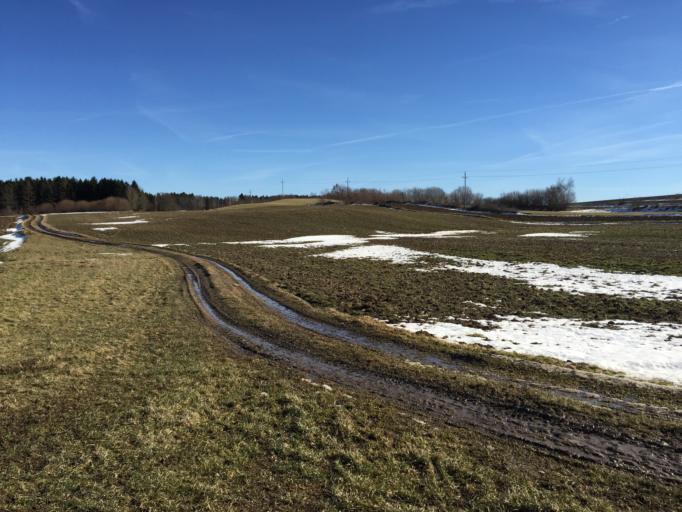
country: AT
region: Lower Austria
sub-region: Politischer Bezirk Gmund
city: Weitra
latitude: 48.6681
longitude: 14.9402
